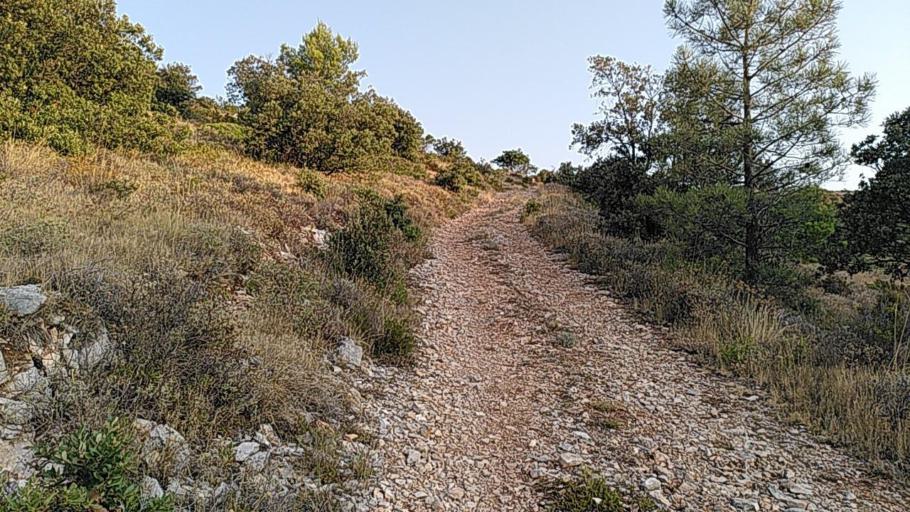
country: HR
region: Splitsko-Dalmatinska
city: Jelsa
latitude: 43.1337
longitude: 16.6804
